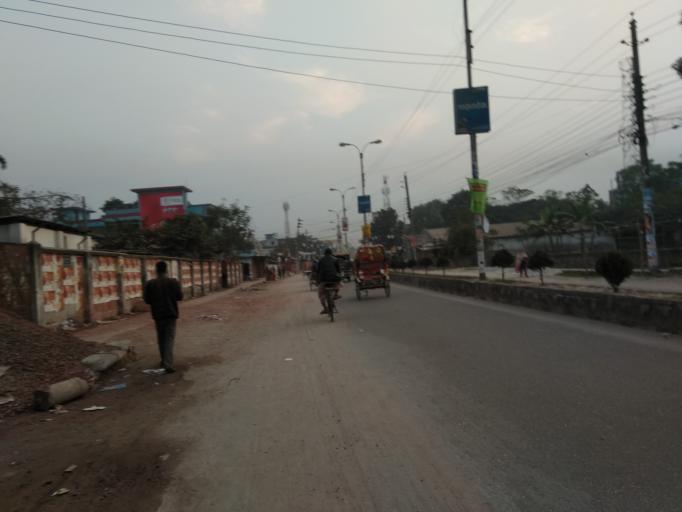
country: BD
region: Rangpur Division
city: Rangpur
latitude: 25.7391
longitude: 89.2547
